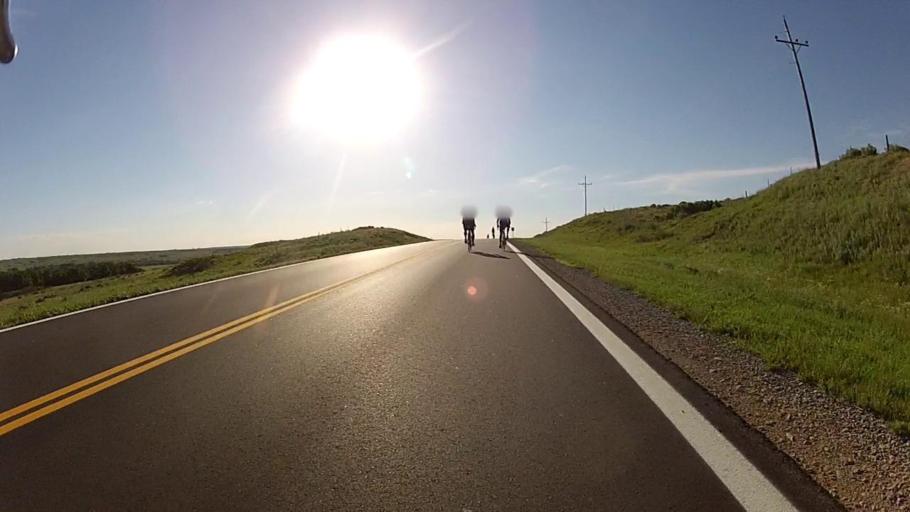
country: US
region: Kansas
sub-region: Comanche County
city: Coldwater
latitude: 37.2816
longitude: -99.0679
